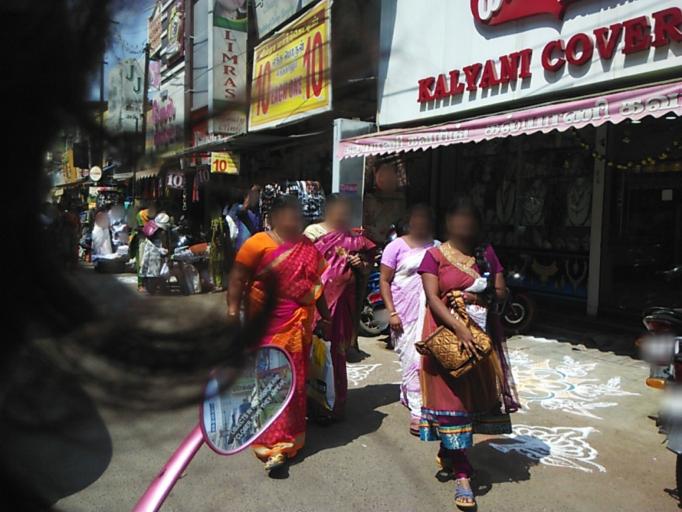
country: IN
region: Tamil Nadu
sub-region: Tiruchchirappalli
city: Tiruchirappalli
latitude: 10.8265
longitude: 78.6957
